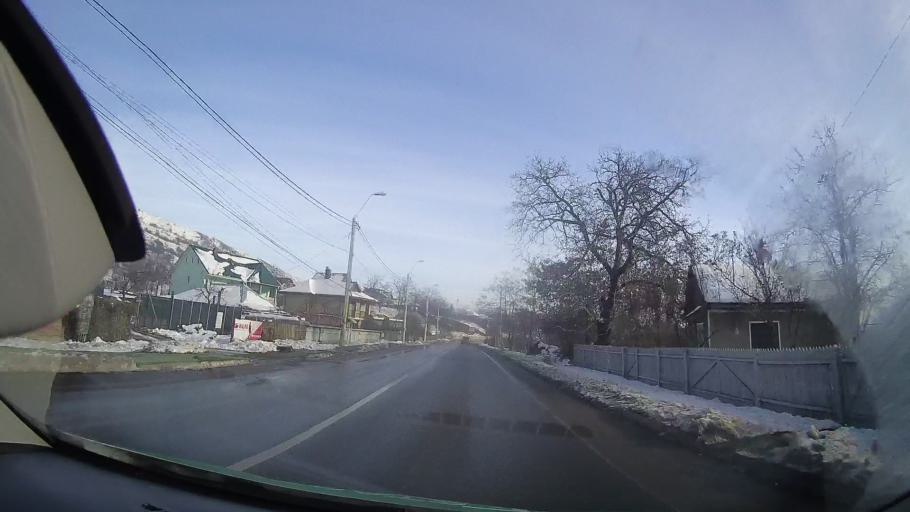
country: RO
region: Neamt
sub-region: Comuna Garcina
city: Garcina
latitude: 46.9729
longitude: 26.3644
